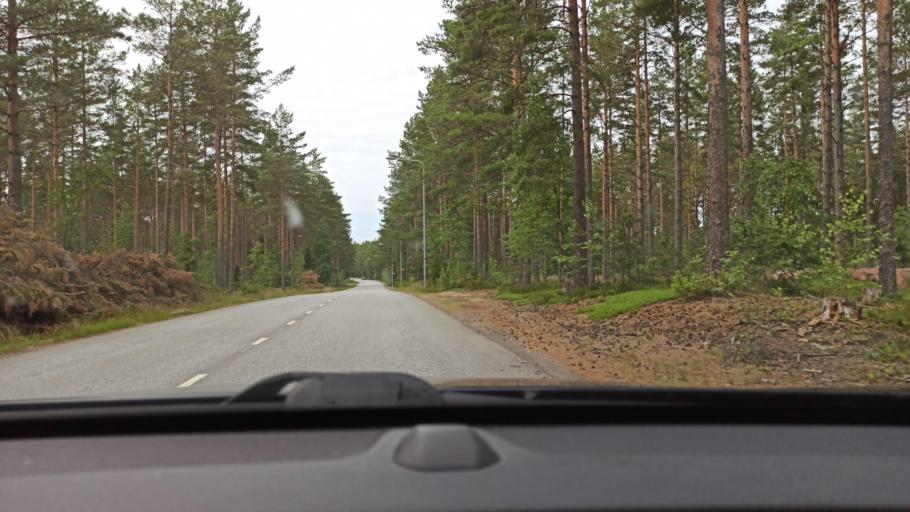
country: FI
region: Satakunta
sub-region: Pori
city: Luvia
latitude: 61.5724
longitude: 21.5324
